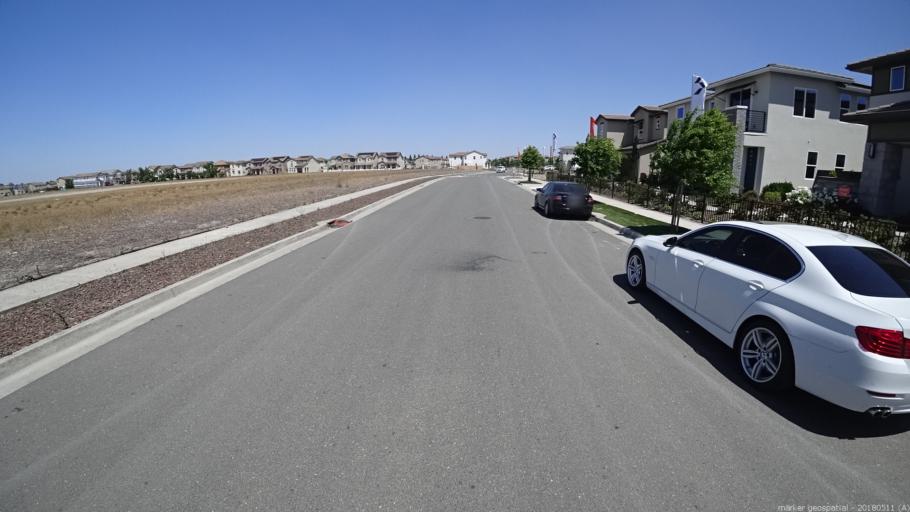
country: US
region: California
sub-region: Sacramento County
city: Rio Linda
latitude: 38.6519
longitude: -121.4975
